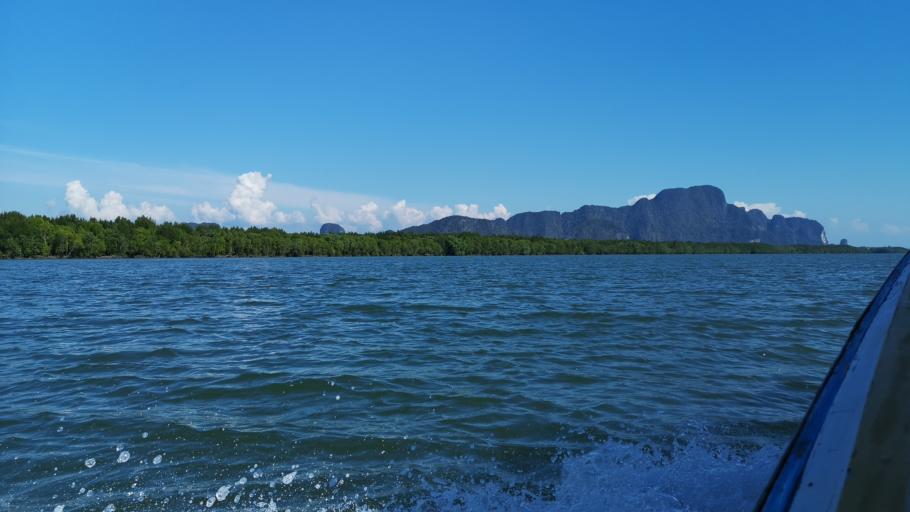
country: TH
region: Phangnga
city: Takua Thung
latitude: 8.3057
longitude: 98.4478
